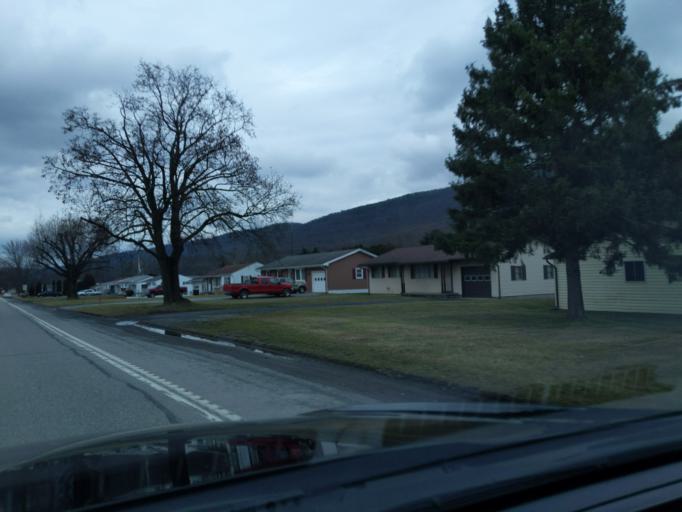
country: US
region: Pennsylvania
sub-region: Blair County
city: Tipton
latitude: 40.6337
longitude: -78.2871
